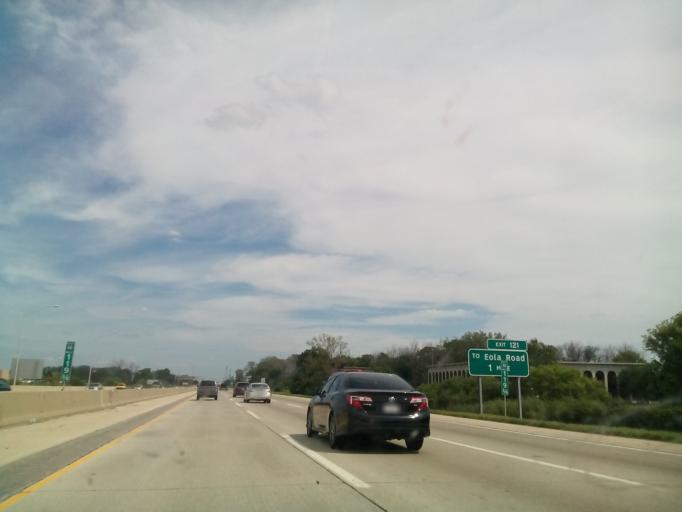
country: US
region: Illinois
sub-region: Kane County
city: North Aurora
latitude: 41.7990
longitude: -88.2729
